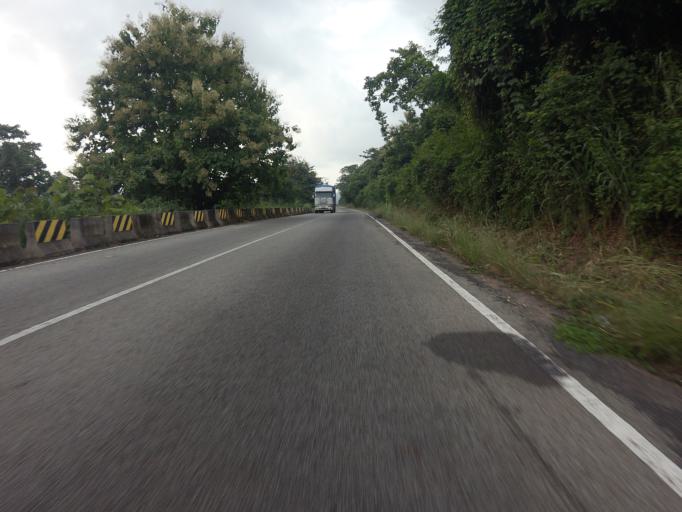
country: GH
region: Volta
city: Ho
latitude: 6.6319
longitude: 0.4637
